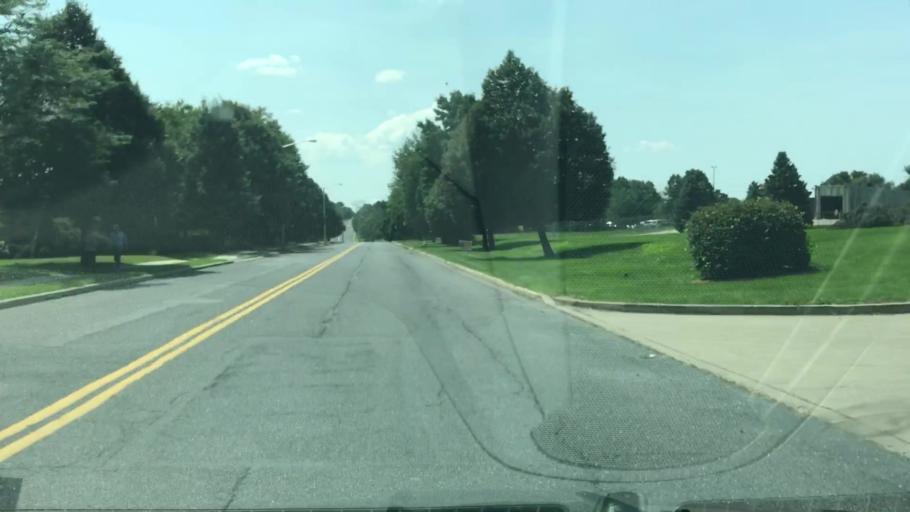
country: US
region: Pennsylvania
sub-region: Northampton County
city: Middletown
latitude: 40.6740
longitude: -75.3649
